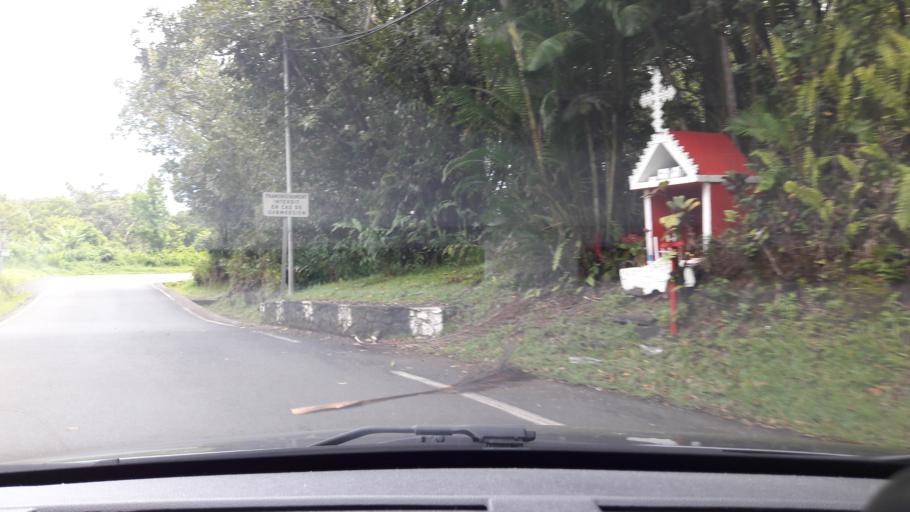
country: RE
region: Reunion
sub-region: Reunion
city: Saint-Benoit
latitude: -21.0855
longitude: 55.6953
